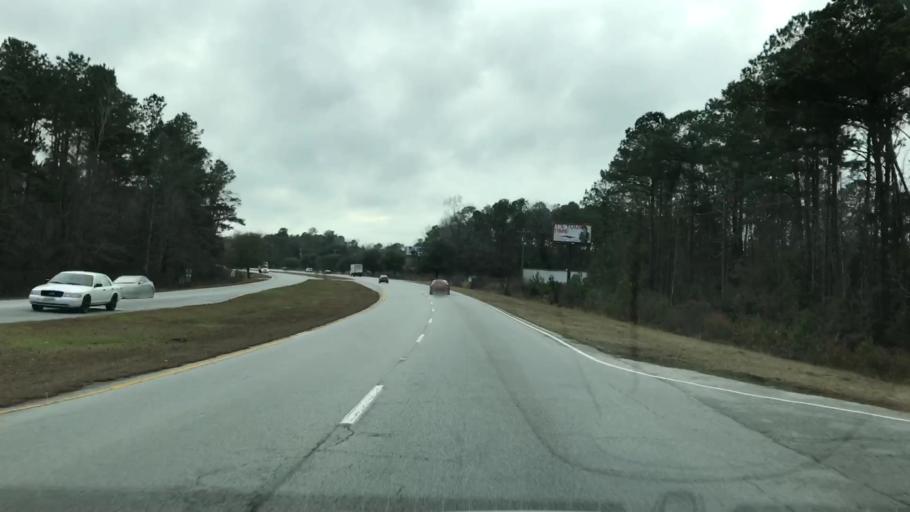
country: US
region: South Carolina
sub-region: Berkeley County
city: Moncks Corner
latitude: 33.1848
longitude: -80.0122
